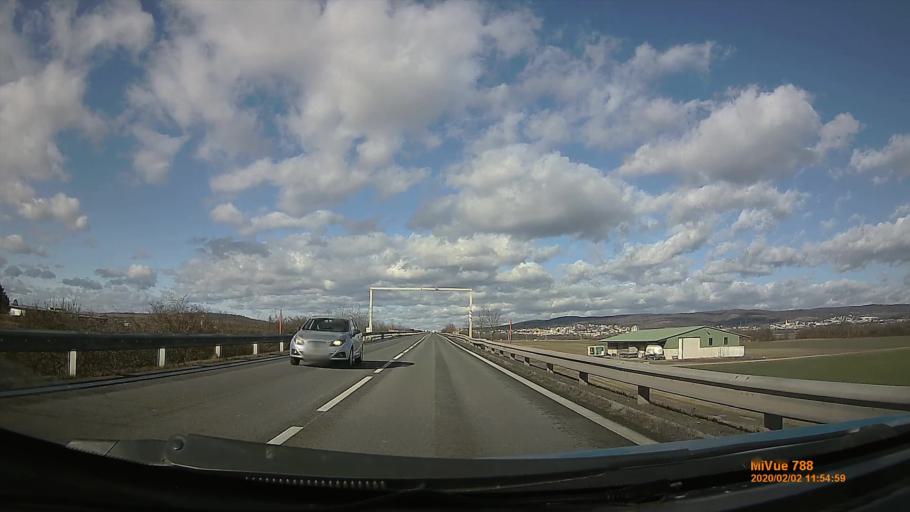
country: AT
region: Burgenland
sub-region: Eisenstadt-Umgebung
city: Wulkaprodersdorf
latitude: 47.8005
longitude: 16.5125
